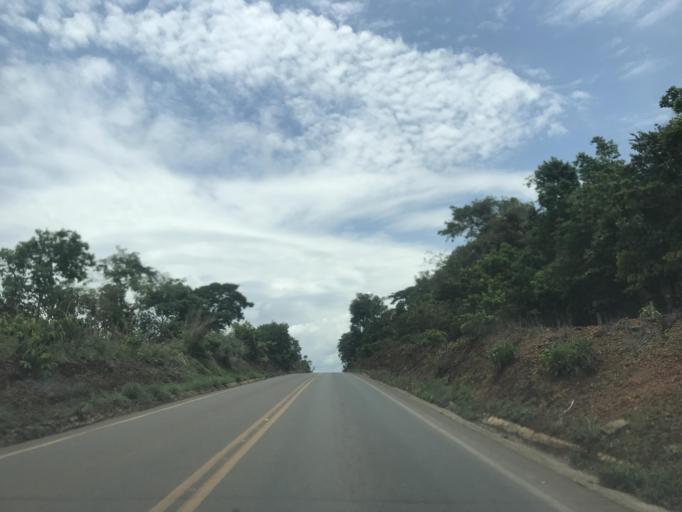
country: BR
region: Goias
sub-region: Vianopolis
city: Vianopolis
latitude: -16.7222
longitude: -48.4084
